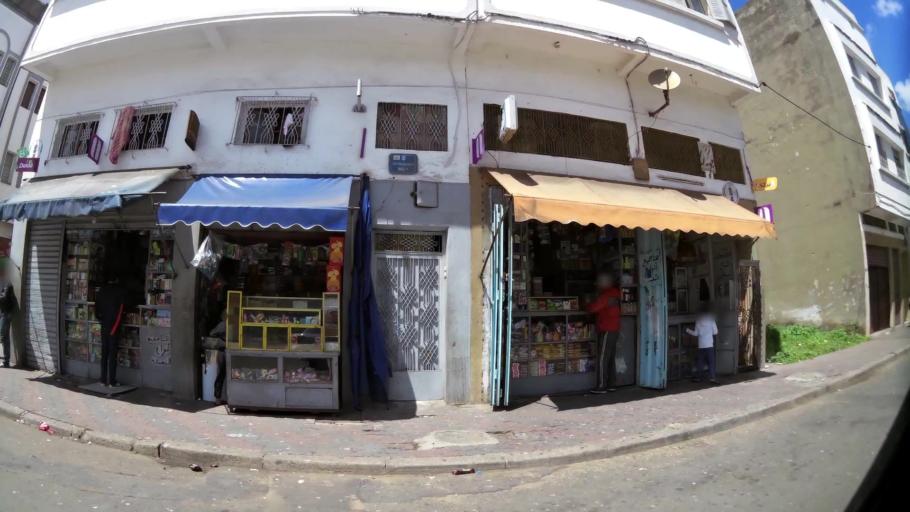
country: MA
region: Grand Casablanca
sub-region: Casablanca
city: Casablanca
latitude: 33.5589
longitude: -7.5836
